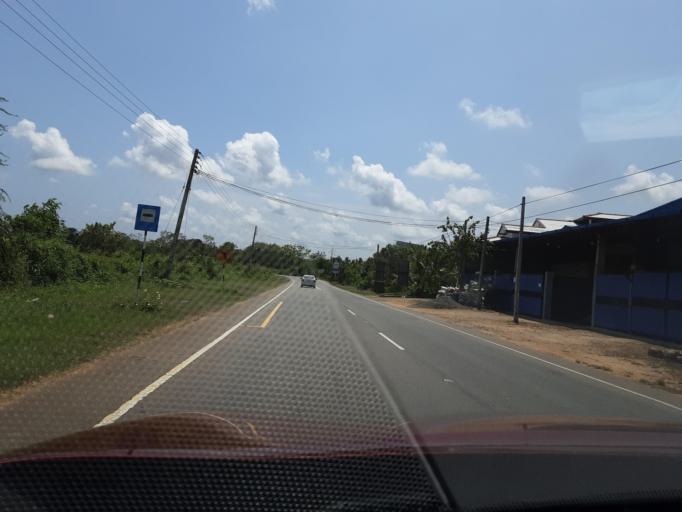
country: LK
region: Southern
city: Tangalla
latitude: 6.2150
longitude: 81.2083
